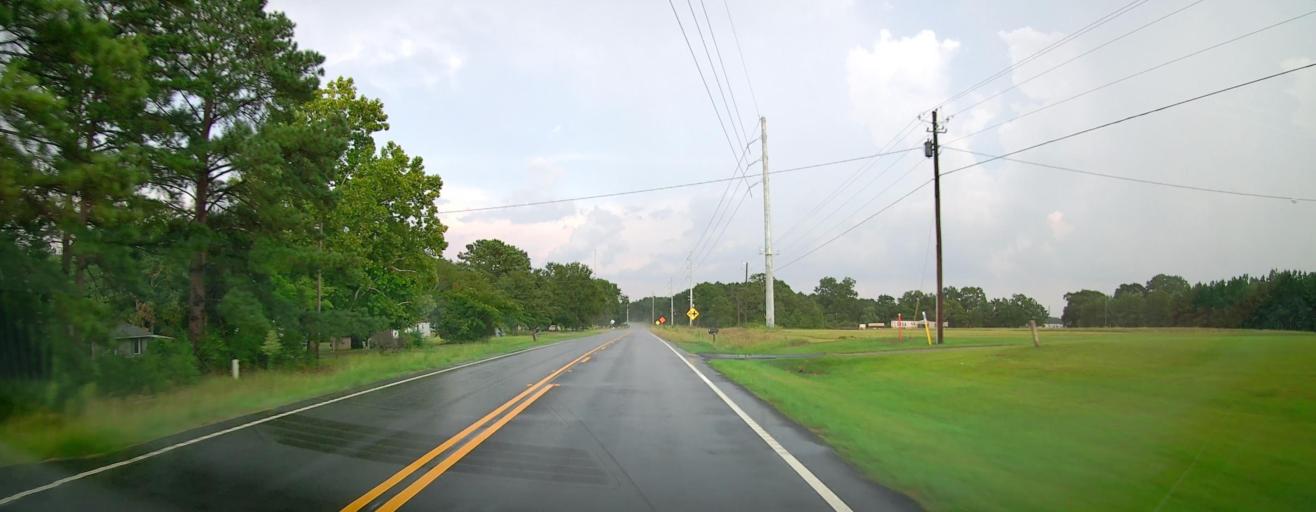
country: US
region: Georgia
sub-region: Twiggs County
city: Jeffersonville
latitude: 32.5764
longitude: -83.2045
